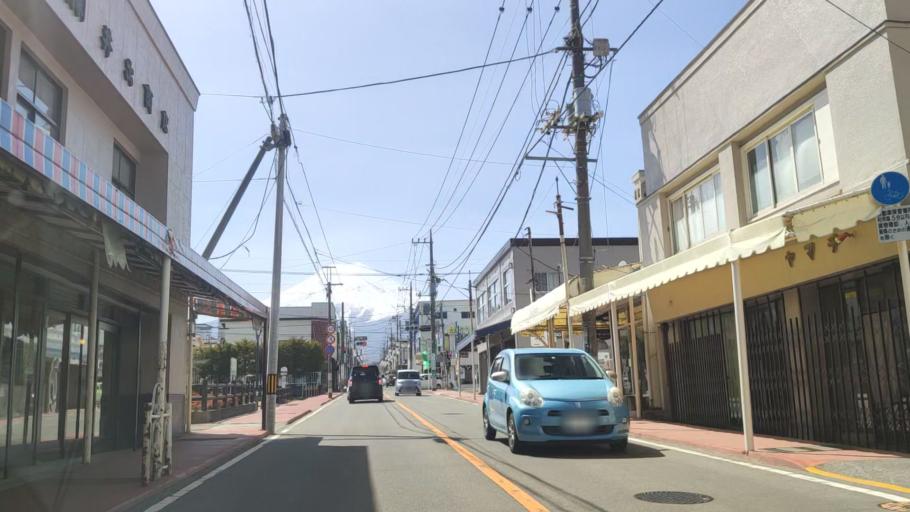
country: JP
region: Yamanashi
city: Fujikawaguchiko
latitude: 35.4906
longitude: 138.8027
